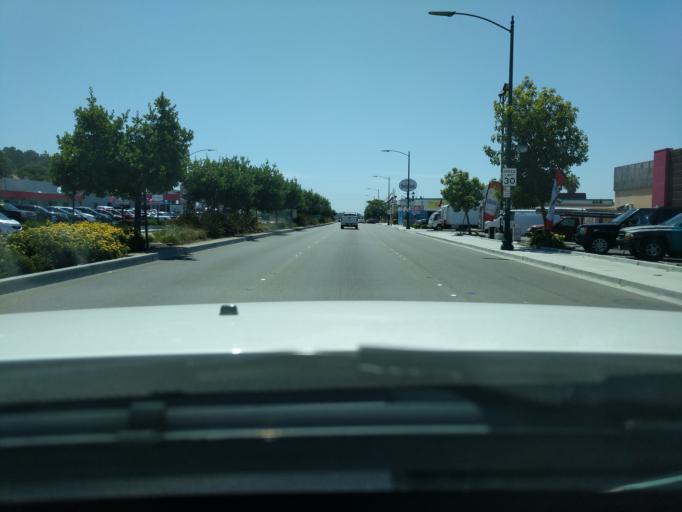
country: US
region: California
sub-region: Alameda County
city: Hayward
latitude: 37.6630
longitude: -122.0762
